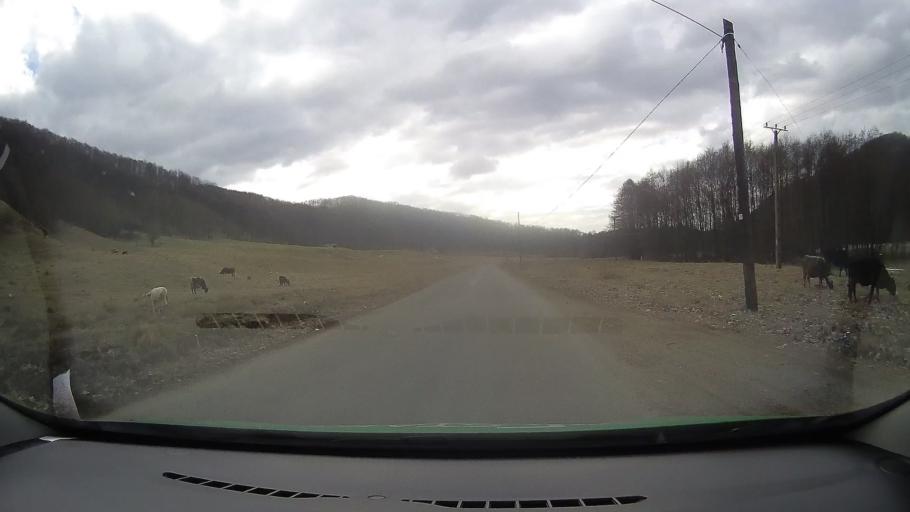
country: RO
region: Dambovita
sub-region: Comuna Visinesti
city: Visinesti
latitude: 45.0938
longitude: 25.5786
